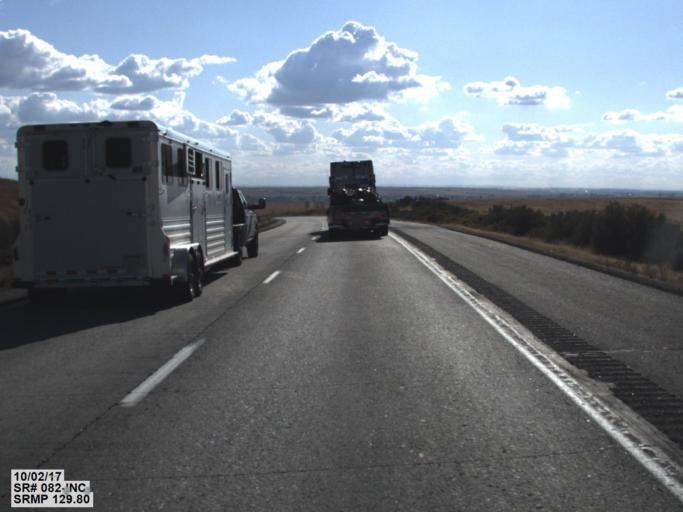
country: US
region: Oregon
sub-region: Umatilla County
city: Umatilla
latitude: 45.9701
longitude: -119.3398
